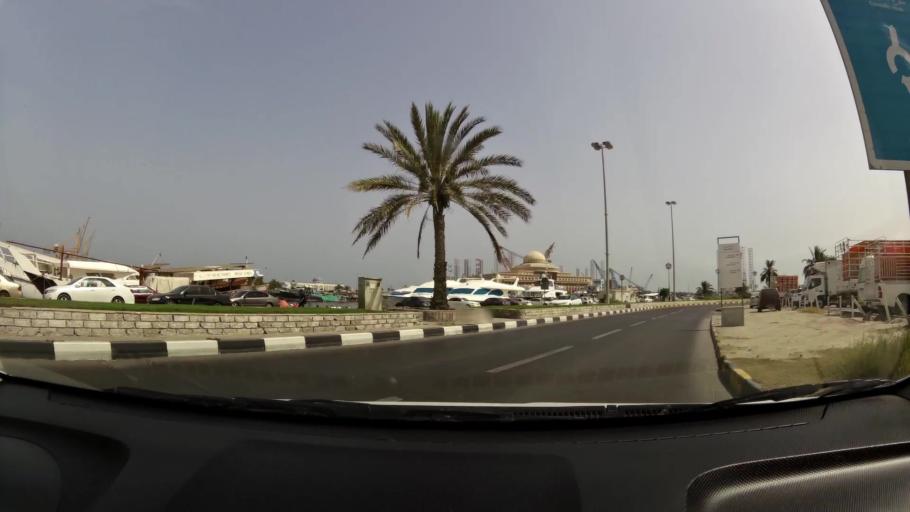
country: AE
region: Ash Shariqah
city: Sharjah
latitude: 25.3560
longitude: 55.3785
